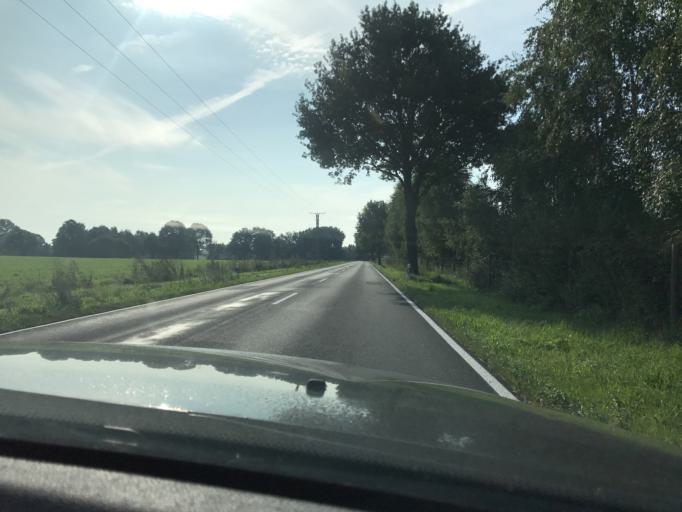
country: DE
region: Lower Saxony
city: Bawinkel
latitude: 52.6653
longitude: 7.4097
